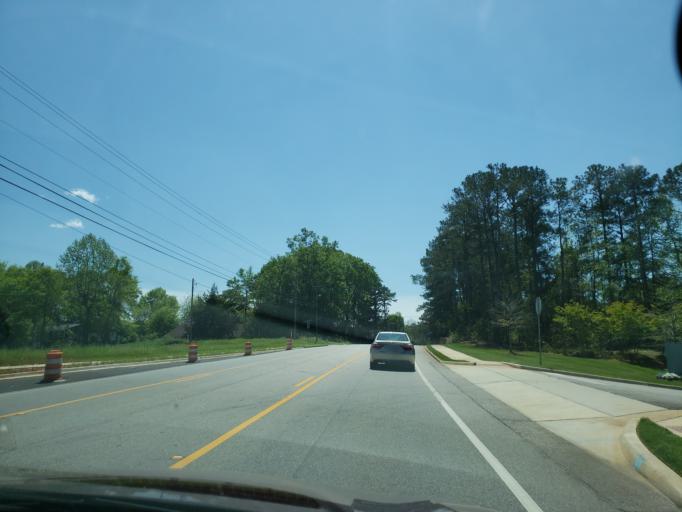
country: US
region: Alabama
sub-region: Lee County
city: Auburn
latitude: 32.6273
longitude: -85.4954
